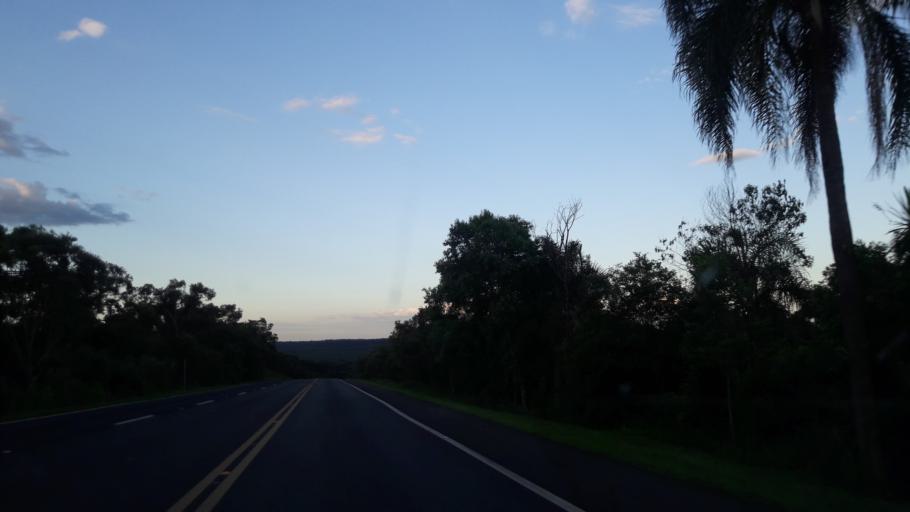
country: BR
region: Parana
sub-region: Irati
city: Irati
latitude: -25.4636
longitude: -50.4625
